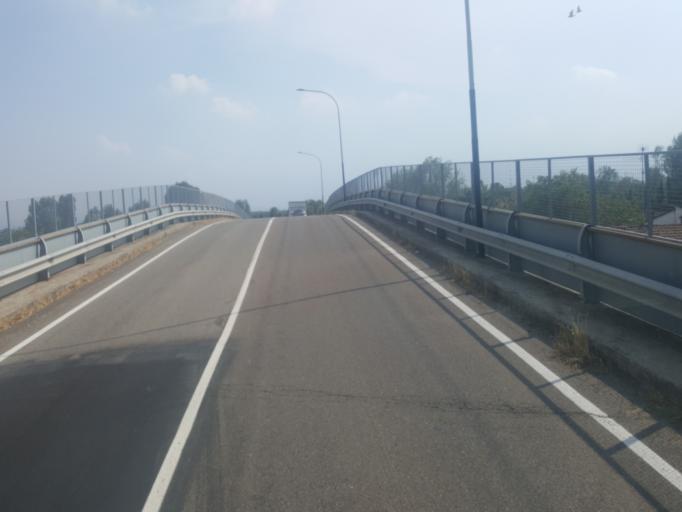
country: IT
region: Emilia-Romagna
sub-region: Provincia di Modena
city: Gaggio
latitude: 44.6262
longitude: 11.0083
